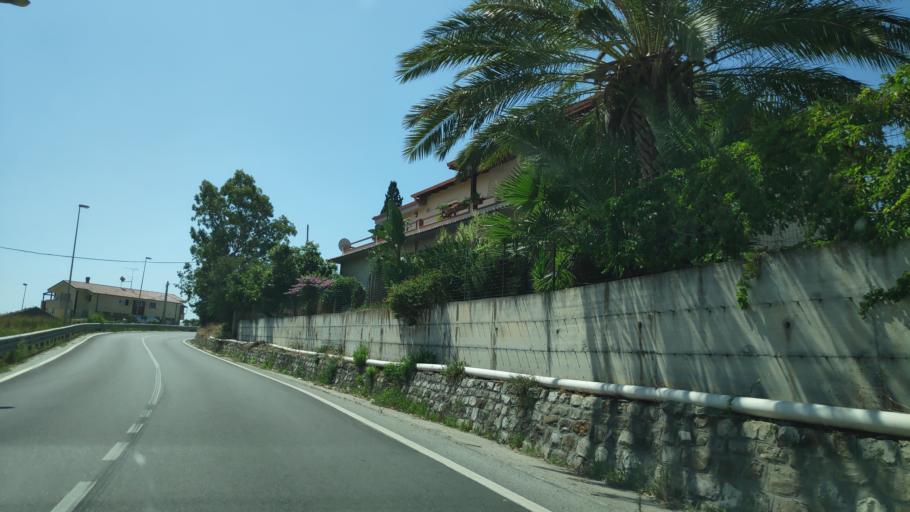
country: IT
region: Calabria
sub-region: Provincia di Reggio Calabria
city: Africo Nuovo
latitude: 38.0175
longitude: 16.1335
